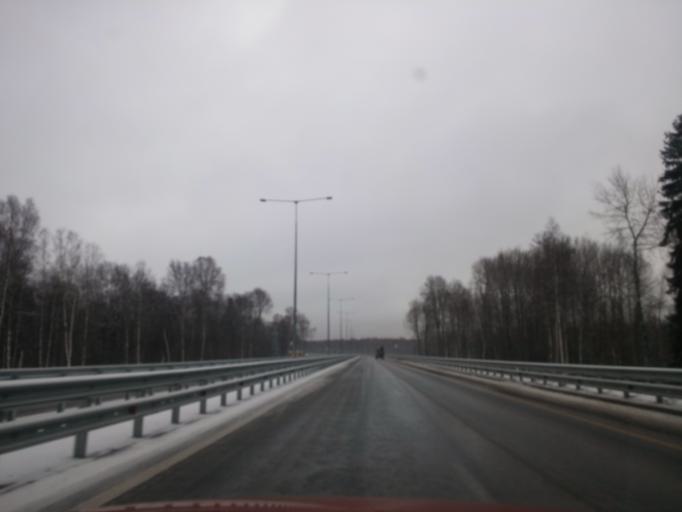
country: RU
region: Tverskaya
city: Likhoslavl'
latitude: 56.9625
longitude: 35.4770
